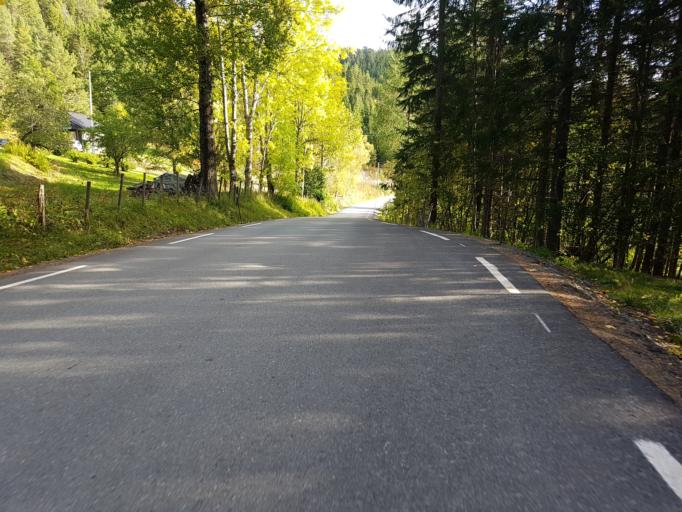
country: NO
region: Sor-Trondelag
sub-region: Malvik
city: Malvik
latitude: 63.3575
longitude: 10.6373
